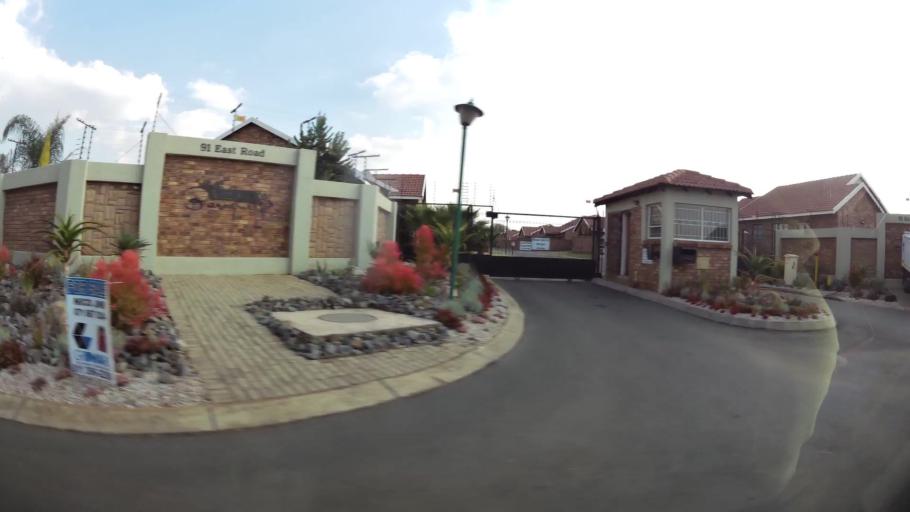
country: ZA
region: Gauteng
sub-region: Ekurhuleni Metropolitan Municipality
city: Benoni
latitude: -26.1110
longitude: 28.2870
